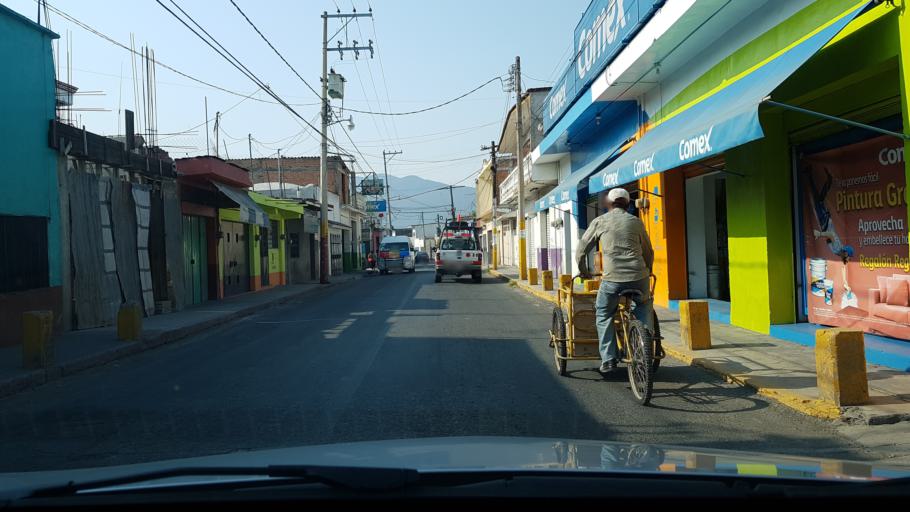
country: MX
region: Morelos
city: Tlaquiltenango
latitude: 18.6323
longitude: -99.1621
